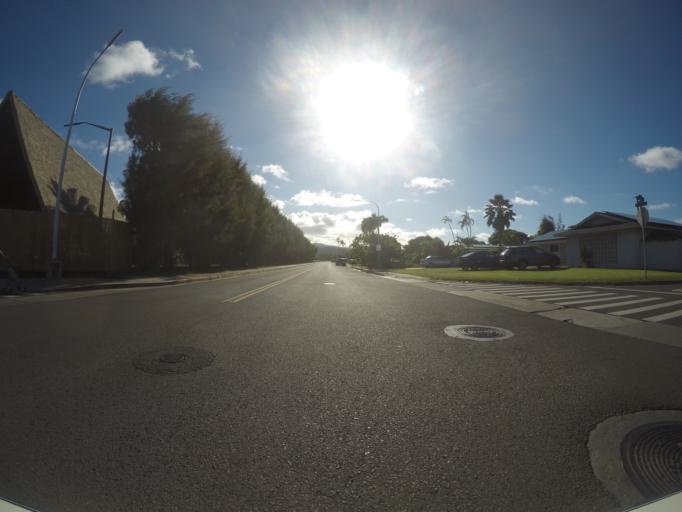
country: US
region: Hawaii
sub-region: Honolulu County
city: La'ie
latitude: 21.6439
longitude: -157.9211
